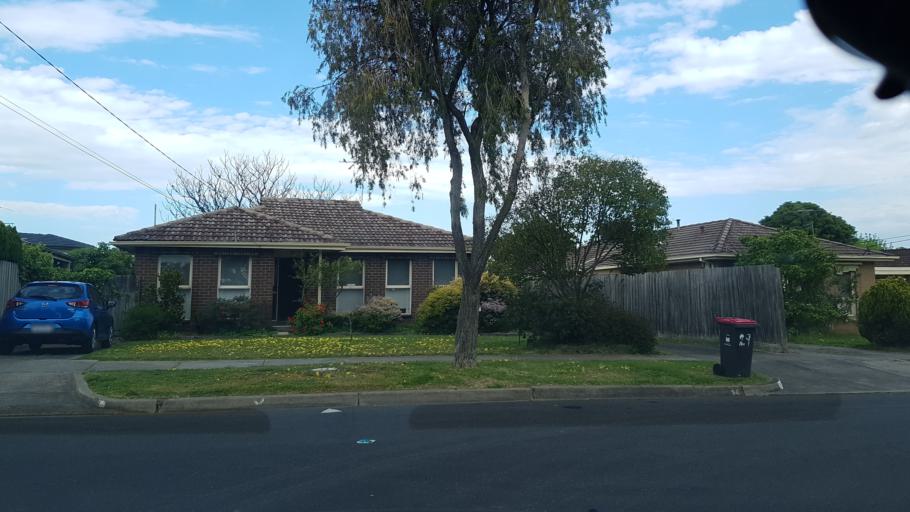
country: AU
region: Victoria
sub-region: Monash
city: Mulgrave
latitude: -37.9160
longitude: 145.1738
